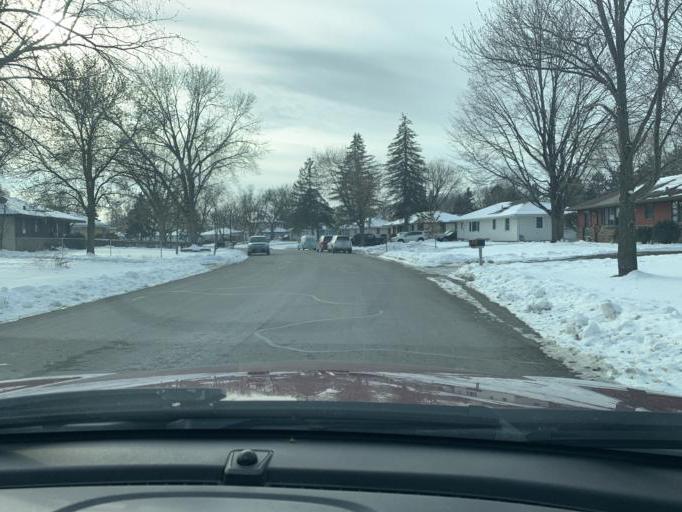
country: US
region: Minnesota
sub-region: Washington County
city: Saint Paul Park
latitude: 44.8287
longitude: -92.9724
